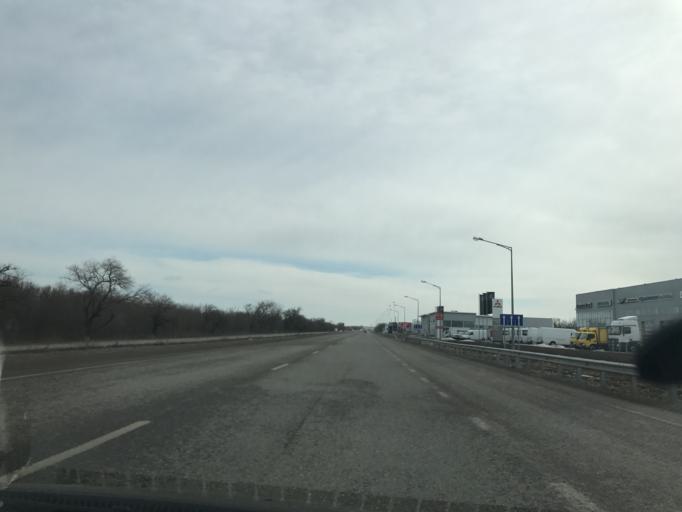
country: RU
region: Stavropol'skiy
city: Andzhiyevskiy
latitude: 44.2230
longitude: 43.0610
